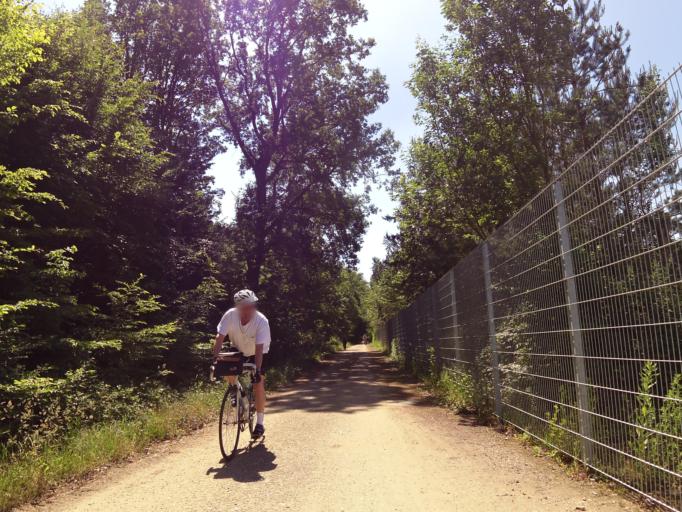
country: DE
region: Hesse
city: Morfelden-Walldorf
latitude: 50.0120
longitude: 8.6263
